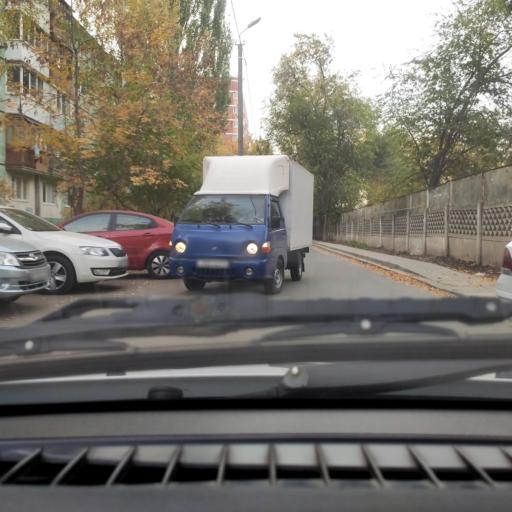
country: RU
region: Samara
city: Tol'yatti
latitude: 53.5046
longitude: 49.4175
